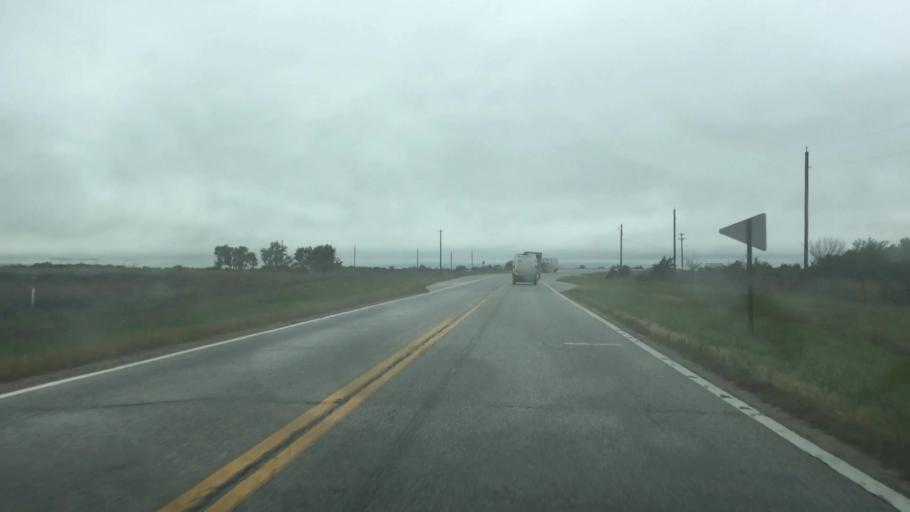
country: US
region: Kansas
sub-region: Anderson County
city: Garnett
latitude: 38.1649
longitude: -95.2962
